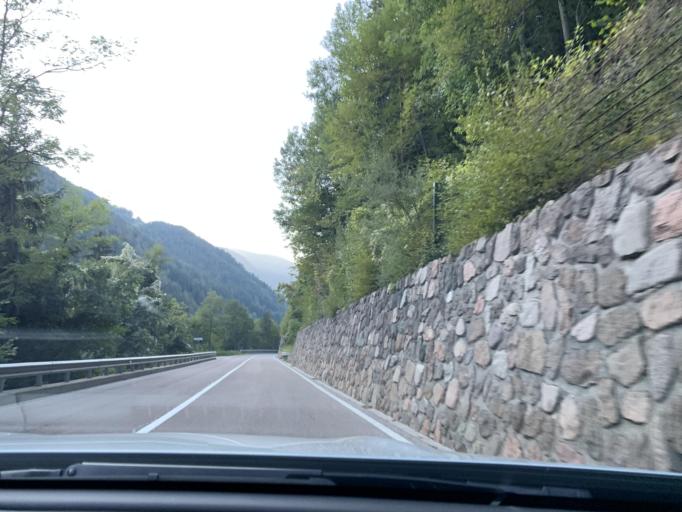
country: IT
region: Trentino-Alto Adige
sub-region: Bolzano
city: Nova Ponente
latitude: 46.4447
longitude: 11.4600
